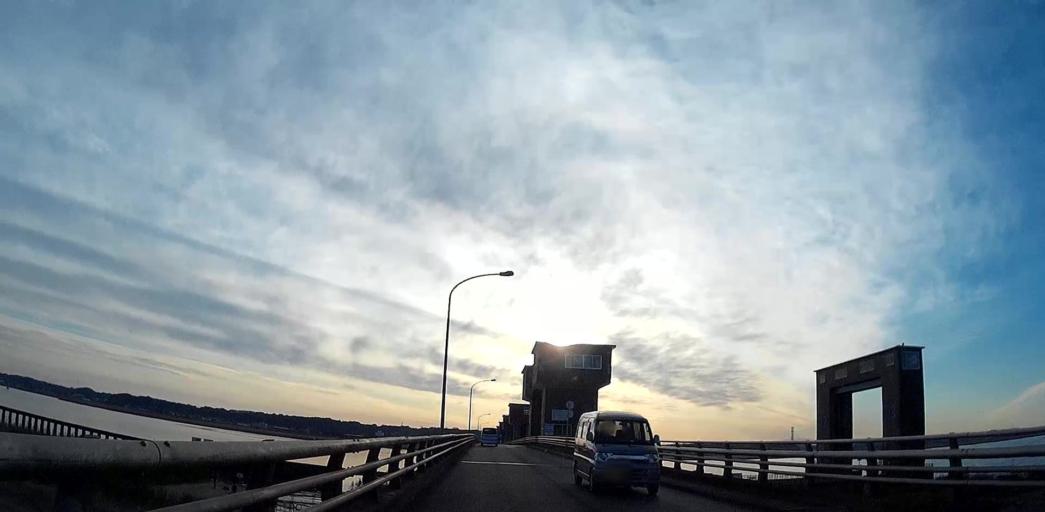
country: JP
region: Chiba
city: Omigawa
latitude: 35.8393
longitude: 140.7060
